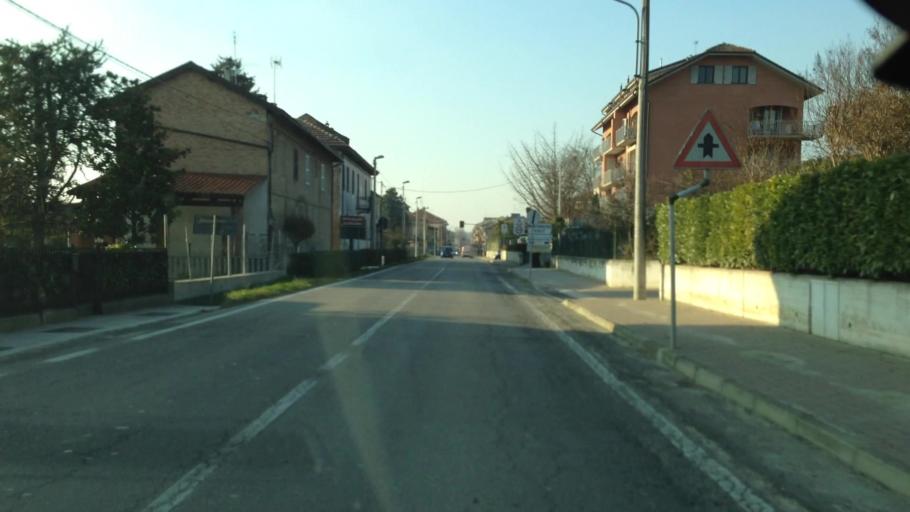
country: IT
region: Piedmont
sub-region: Provincia di Asti
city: Montegrosso
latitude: 44.8176
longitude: 8.2466
